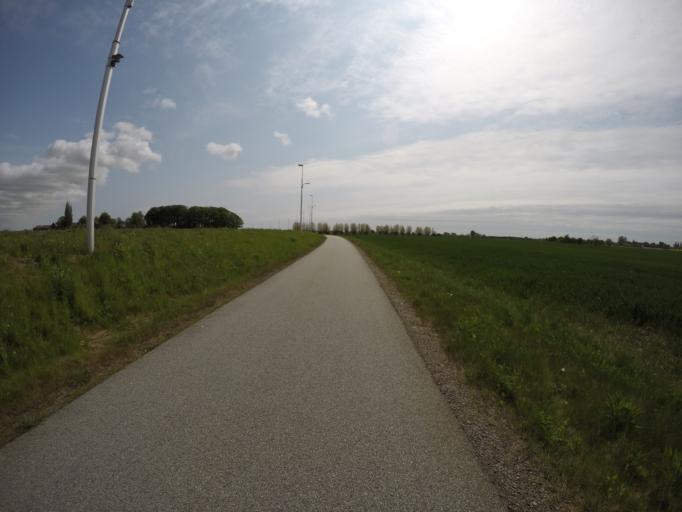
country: SE
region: Skane
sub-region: Malmo
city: Bunkeflostrand
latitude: 55.5428
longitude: 12.9804
